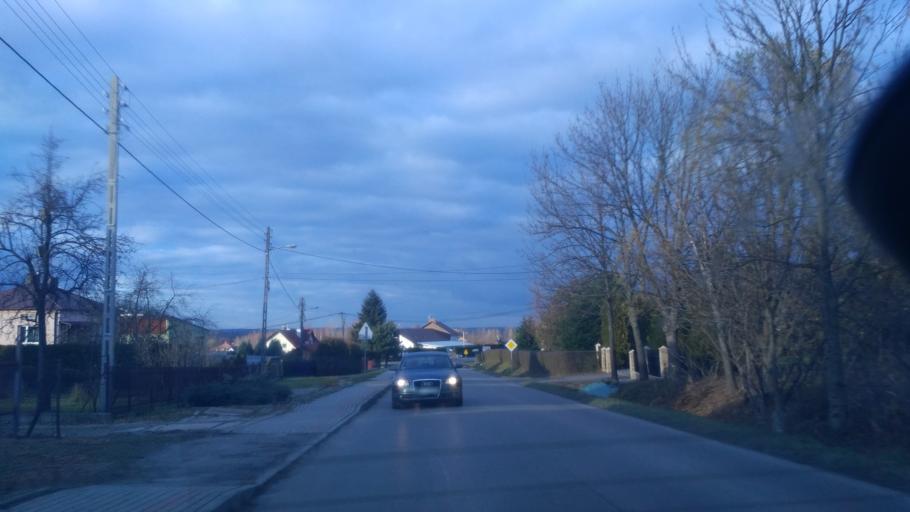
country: PL
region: Subcarpathian Voivodeship
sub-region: Powiat rzeszowski
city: Krasne
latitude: 50.0598
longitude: 22.1194
